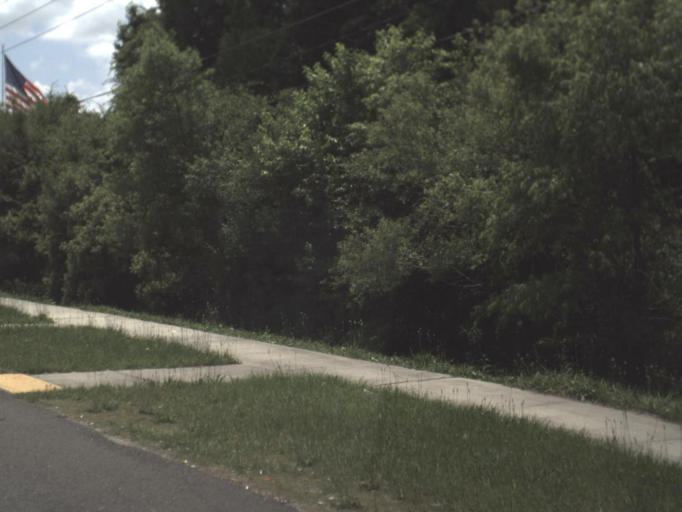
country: US
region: Florida
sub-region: Clay County
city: Bellair-Meadowbrook Terrace
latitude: 30.2178
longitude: -81.7371
